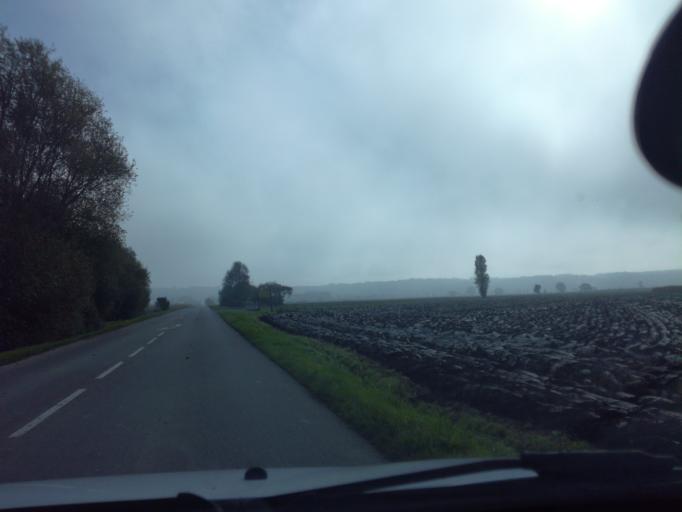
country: FR
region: Brittany
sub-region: Departement d'Ille-et-Vilaine
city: Saint-Broladre
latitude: 48.5987
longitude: -1.6777
